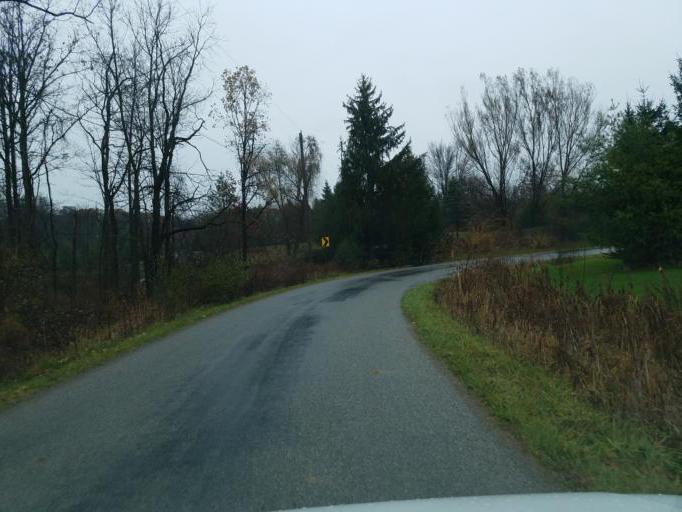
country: US
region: Ohio
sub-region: Knox County
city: Centerburg
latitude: 40.3685
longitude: -82.6695
